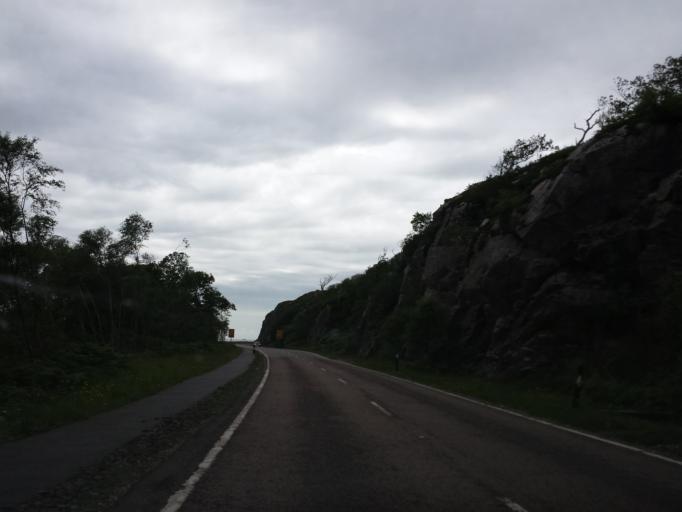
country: GB
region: Scotland
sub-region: Argyll and Bute
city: Isle Of Mull
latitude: 56.8949
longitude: -5.7504
